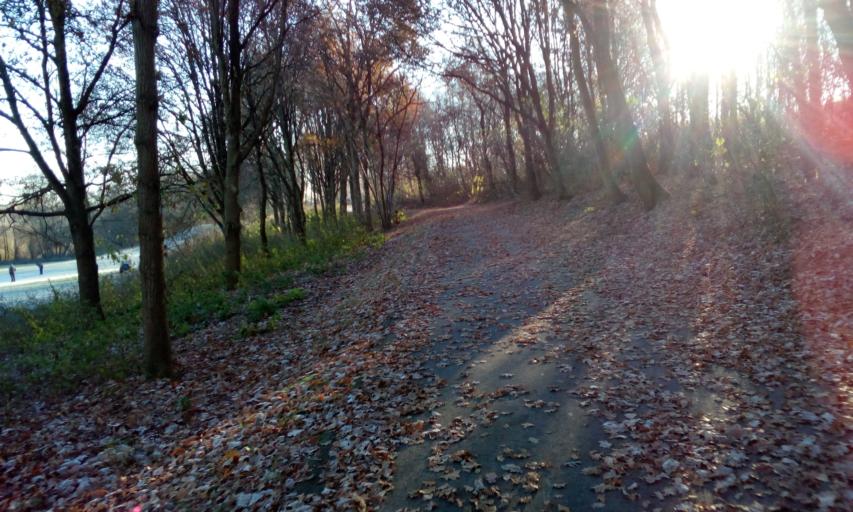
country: NL
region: South Holland
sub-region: Gemeente Lansingerland
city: Bergschenhoek
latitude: 51.9711
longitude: 4.5274
